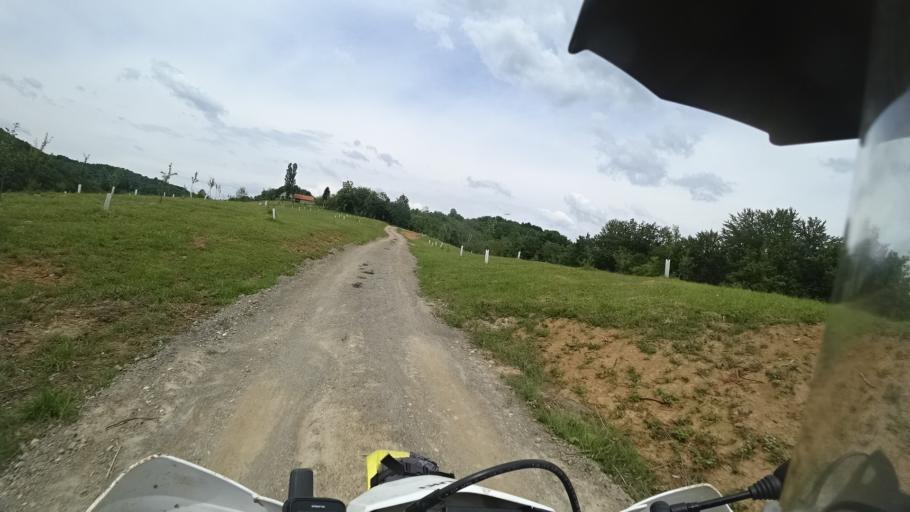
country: HR
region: Karlovacka
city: Vojnic
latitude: 45.2445
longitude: 15.6546
